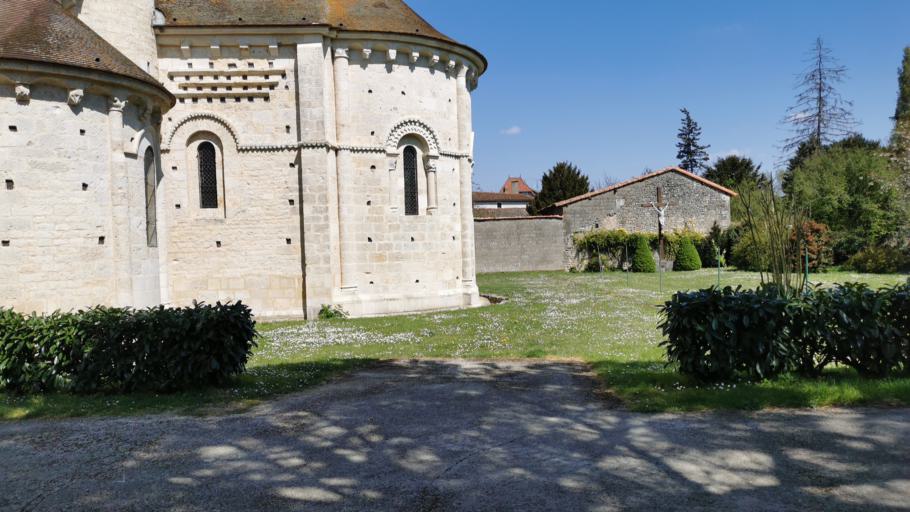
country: FR
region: Poitou-Charentes
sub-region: Departement de la Vienne
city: Civray
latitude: 46.1479
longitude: 0.2972
